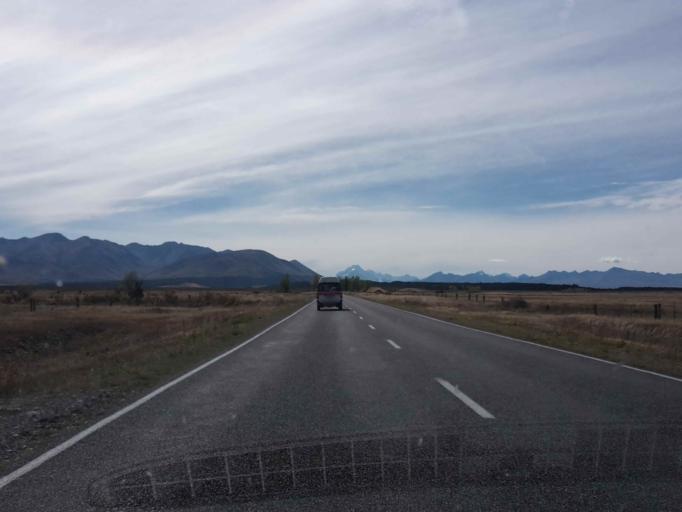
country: NZ
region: Canterbury
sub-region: Timaru District
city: Pleasant Point
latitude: -44.2267
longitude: 170.1163
